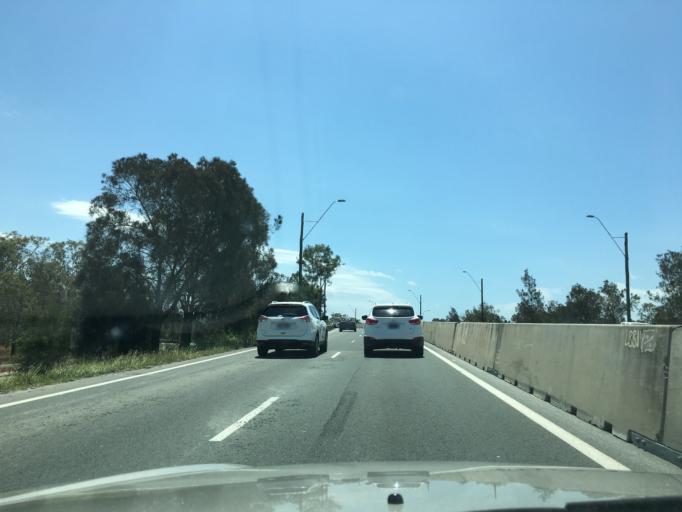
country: AU
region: Queensland
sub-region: Brisbane
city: Deagon
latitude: -27.3437
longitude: 153.0766
